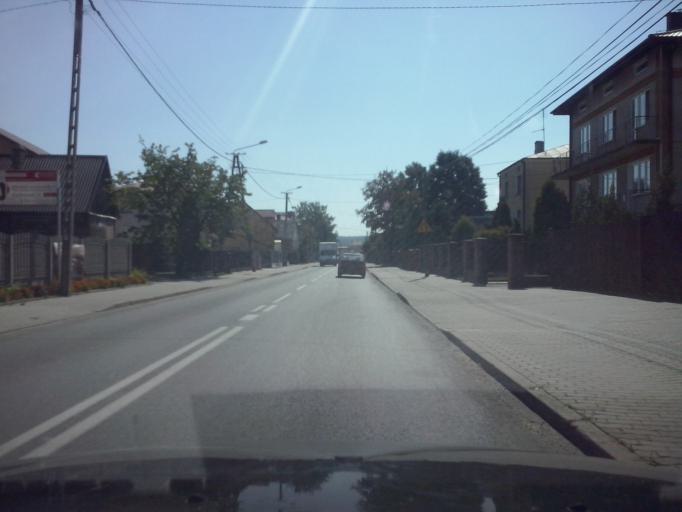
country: PL
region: Swietokrzyskie
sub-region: Powiat kielecki
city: Daleszyce
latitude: 50.8034
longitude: 20.8035
